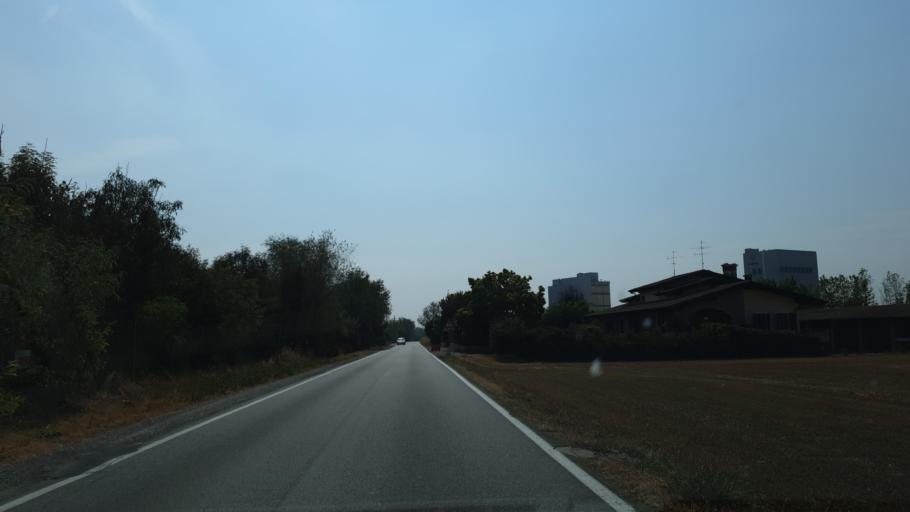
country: IT
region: Lombardy
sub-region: Provincia di Brescia
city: Montirone
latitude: 45.4351
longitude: 10.2576
